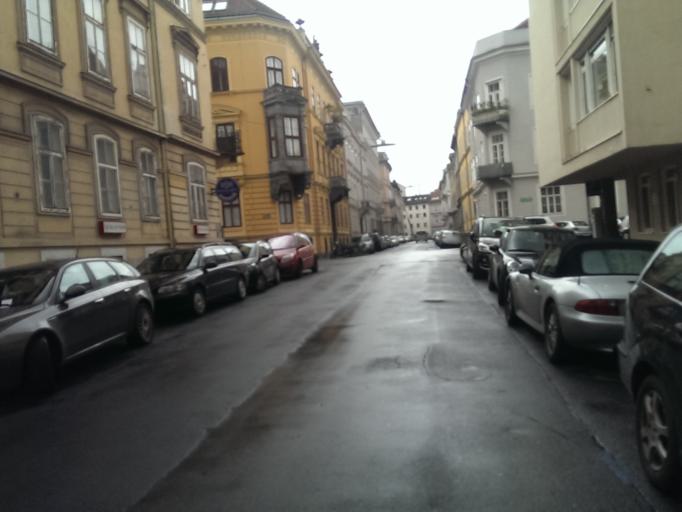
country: AT
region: Styria
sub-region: Graz Stadt
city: Graz
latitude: 47.0706
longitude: 15.4499
